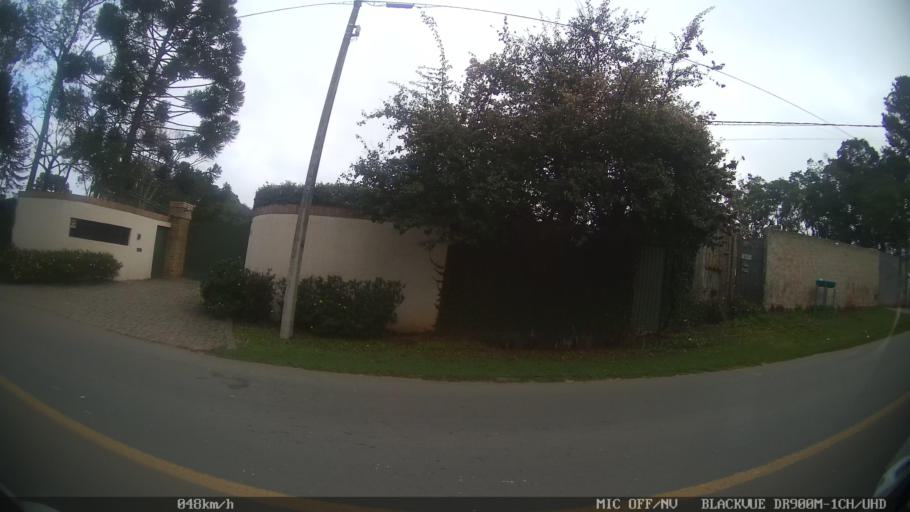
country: BR
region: Parana
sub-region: Almirante Tamandare
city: Almirante Tamandare
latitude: -25.3707
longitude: -49.3221
